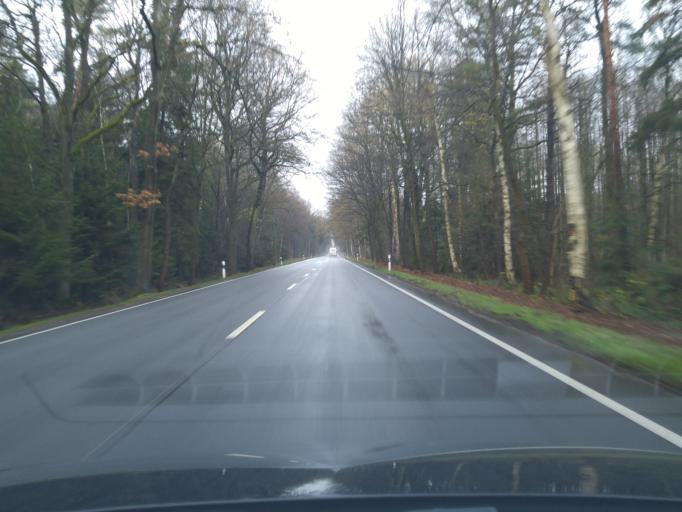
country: DE
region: Lower Saxony
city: Dedelstorf
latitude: 52.6962
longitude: 10.4753
